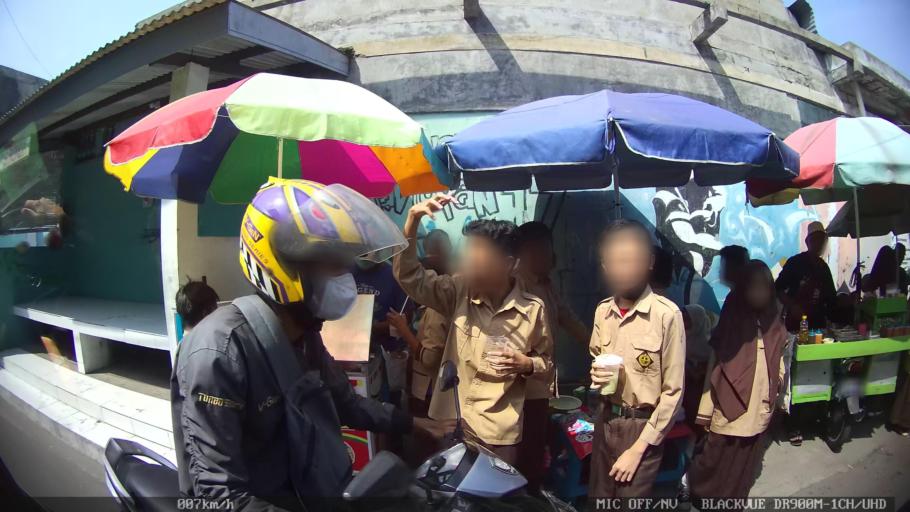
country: ID
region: Daerah Istimewa Yogyakarta
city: Yogyakarta
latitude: -7.8055
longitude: 110.3906
